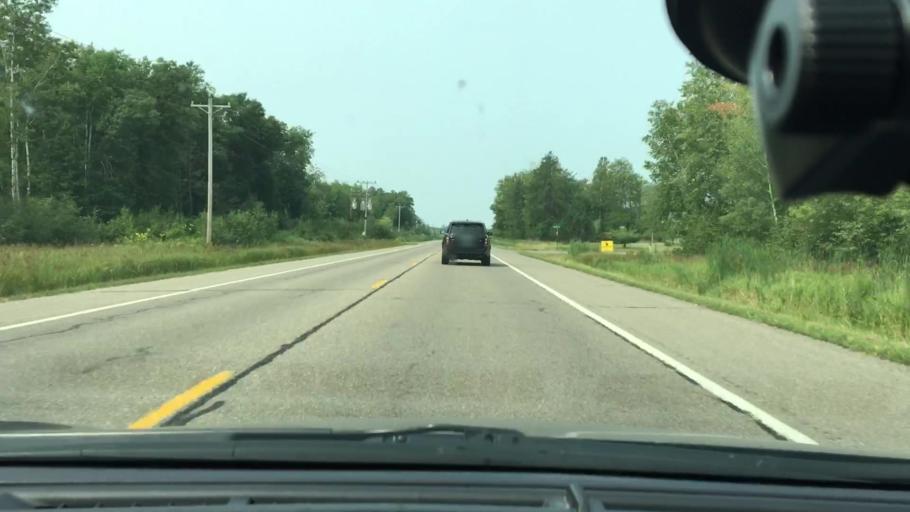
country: US
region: Minnesota
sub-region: Crow Wing County
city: Brainerd
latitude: 46.3984
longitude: -94.2104
